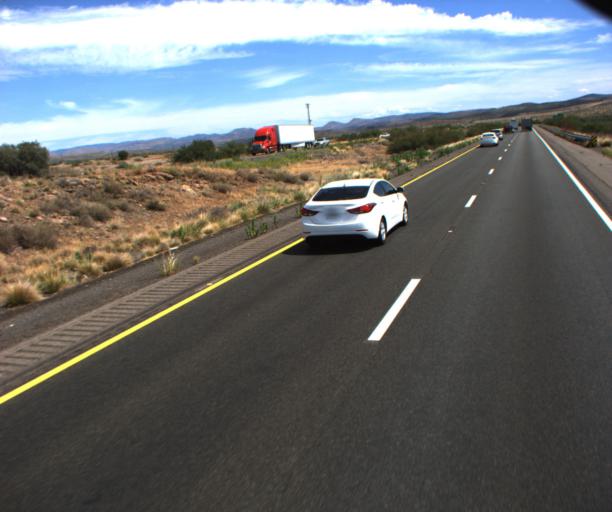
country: US
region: Arizona
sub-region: Yavapai County
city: Cordes Lakes
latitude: 34.3971
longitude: -112.0784
